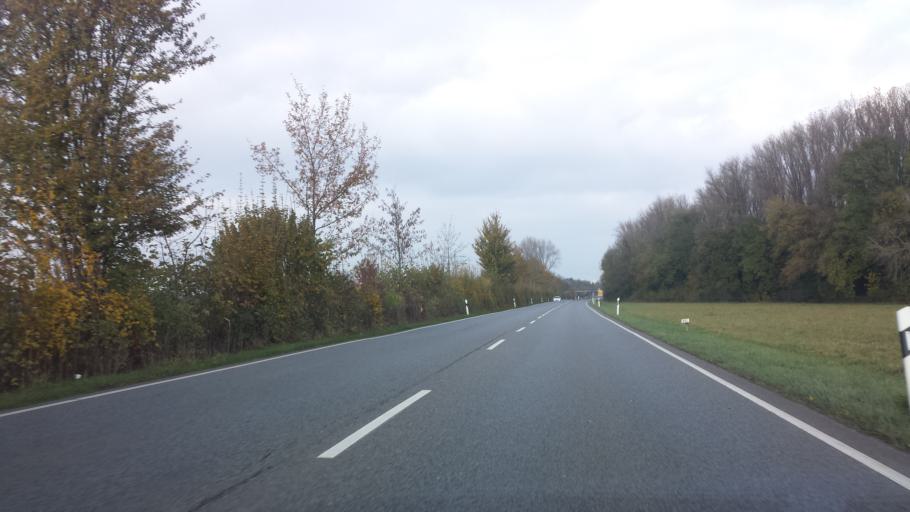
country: DE
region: Baden-Wuerttemberg
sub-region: Karlsruhe Region
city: Wiesloch
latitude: 49.2812
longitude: 8.6670
